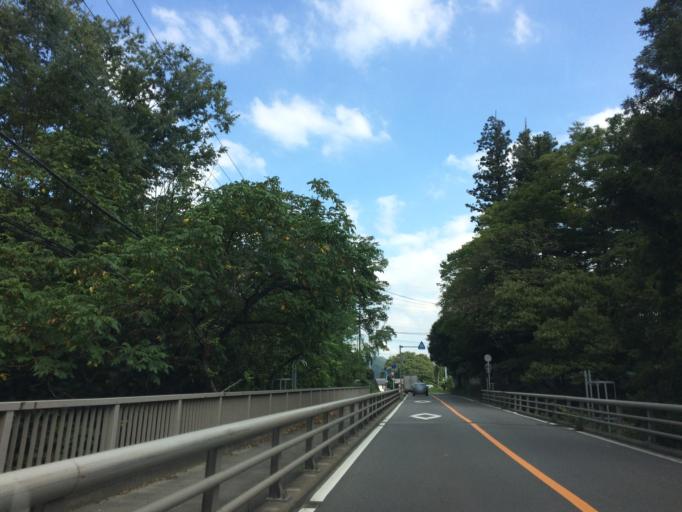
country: JP
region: Gunma
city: Nakanojomachi
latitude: 36.5664
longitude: 138.7511
